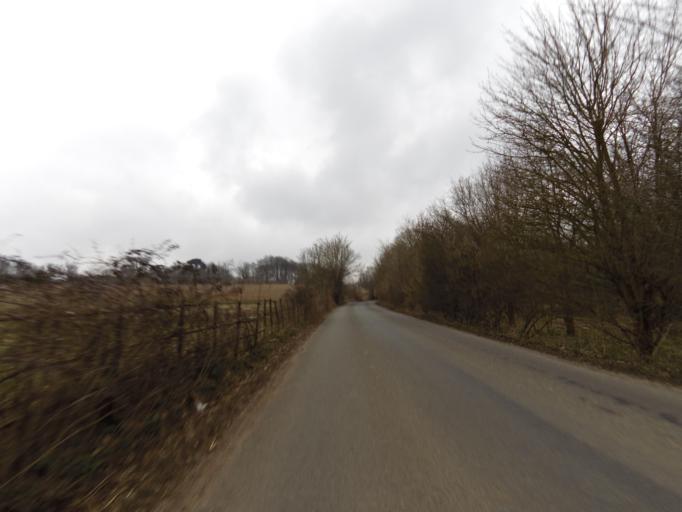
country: GB
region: England
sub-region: Suffolk
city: Wickham Market
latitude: 52.1686
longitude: 1.3538
